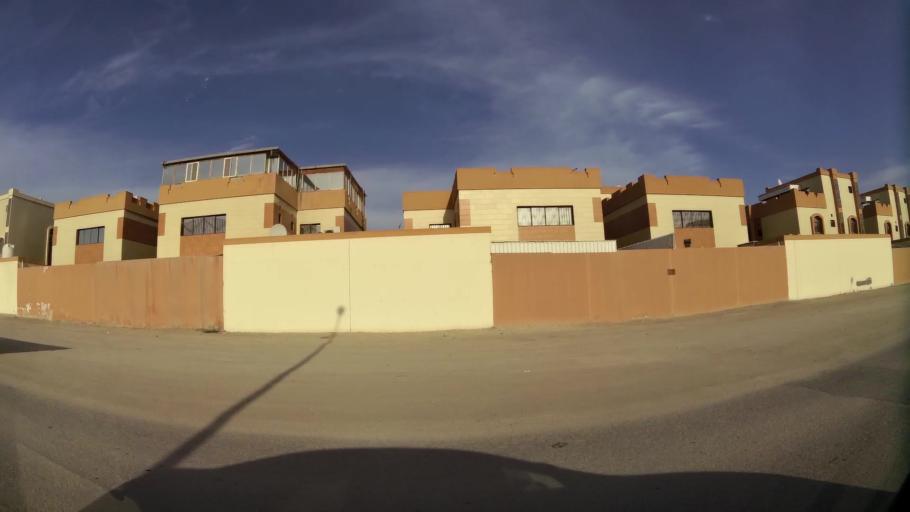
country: QA
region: Al Wakrah
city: Al Wakrah
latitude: 25.1471
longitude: 51.6061
